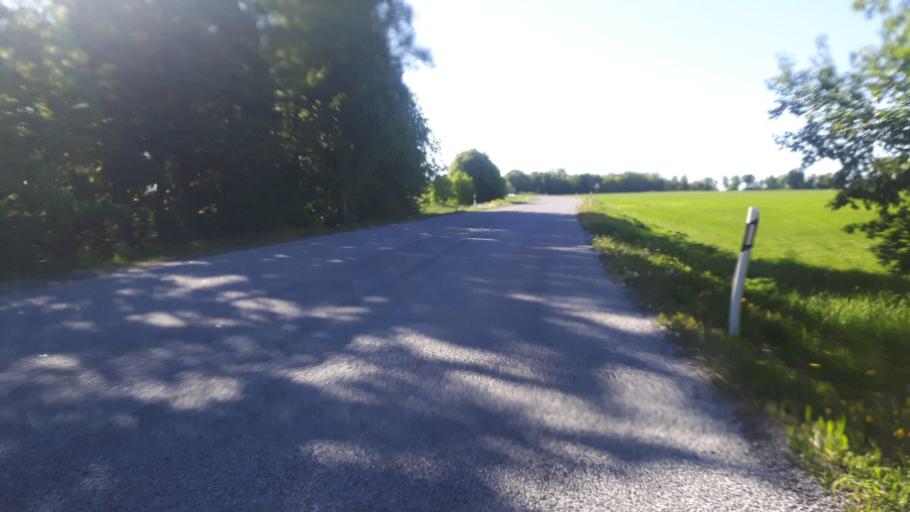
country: EE
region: Ida-Virumaa
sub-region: Kohtla-Jaerve linn
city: Kohtla-Jarve
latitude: 59.4390
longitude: 27.2776
